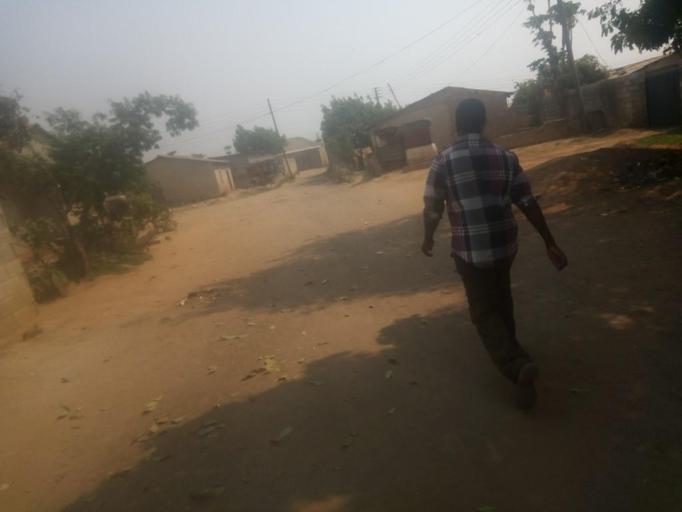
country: ZM
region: Lusaka
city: Lusaka
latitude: -15.3981
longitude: 28.3814
